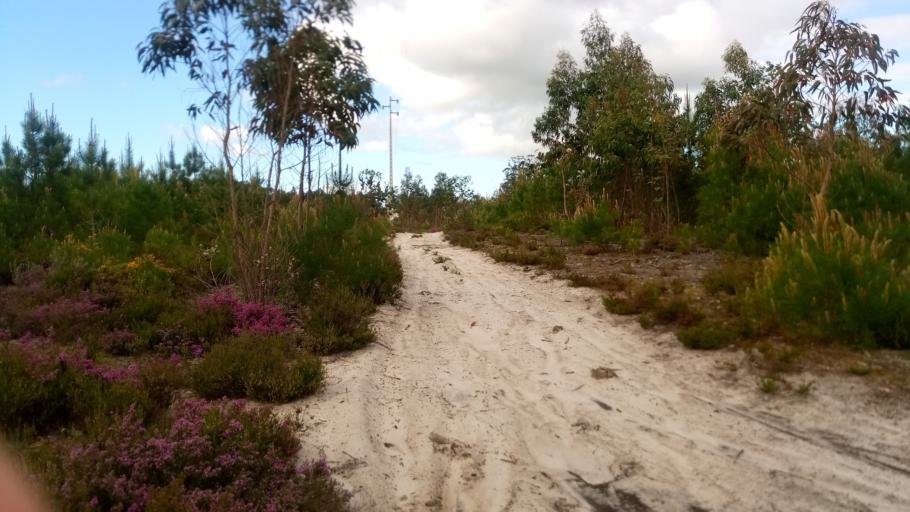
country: PT
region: Leiria
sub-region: Caldas da Rainha
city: Caldas da Rainha
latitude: 39.4415
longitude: -9.1671
